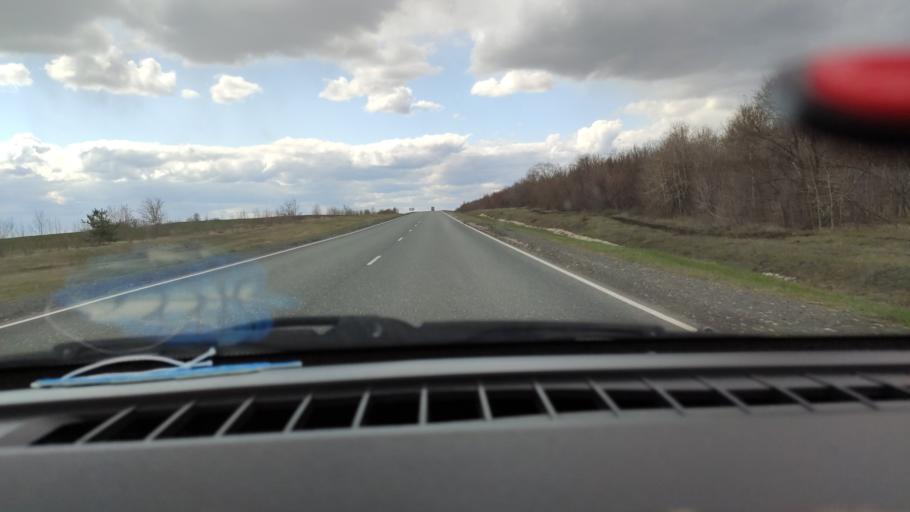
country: RU
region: Saratov
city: Balakovo
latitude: 52.1803
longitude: 47.8412
